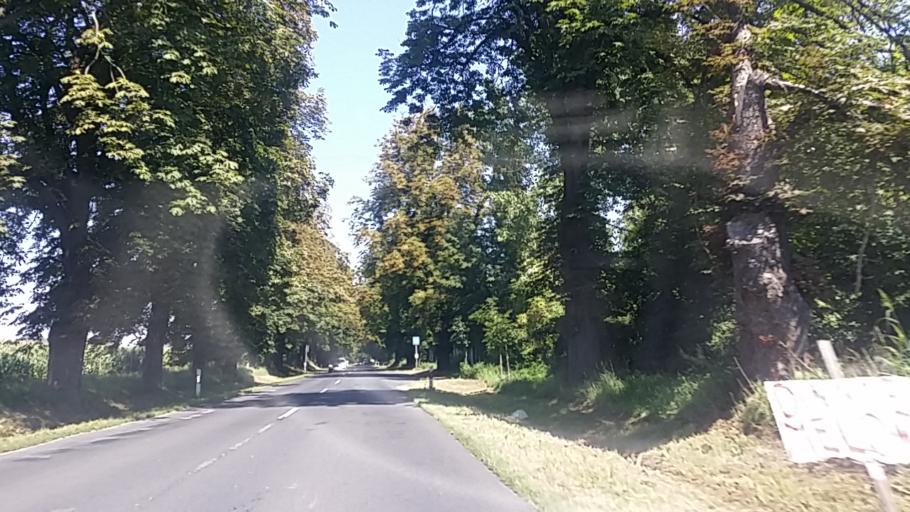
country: HU
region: Zala
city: Keszthely
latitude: 46.7303
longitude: 17.2402
